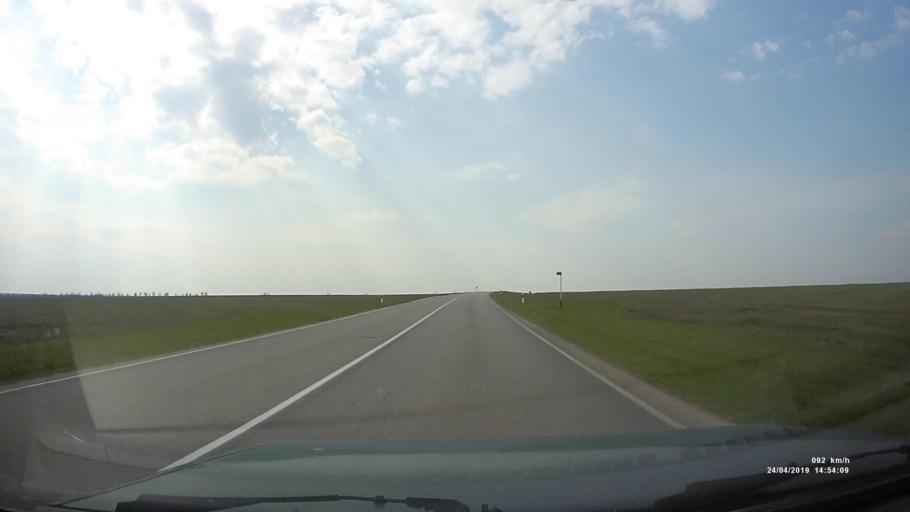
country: RU
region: Rostov
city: Remontnoye
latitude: 46.5328
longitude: 43.6442
